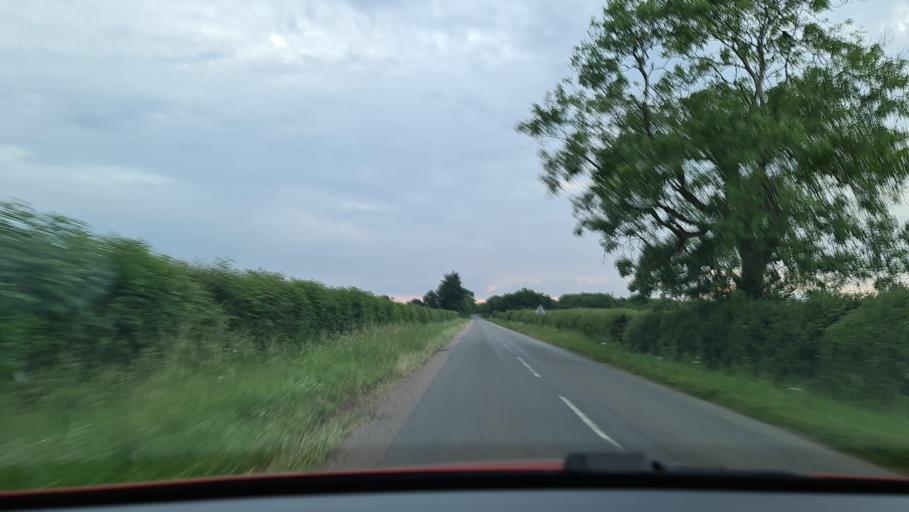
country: GB
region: England
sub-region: Oxfordshire
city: Bicester
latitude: 51.9394
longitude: -1.1364
